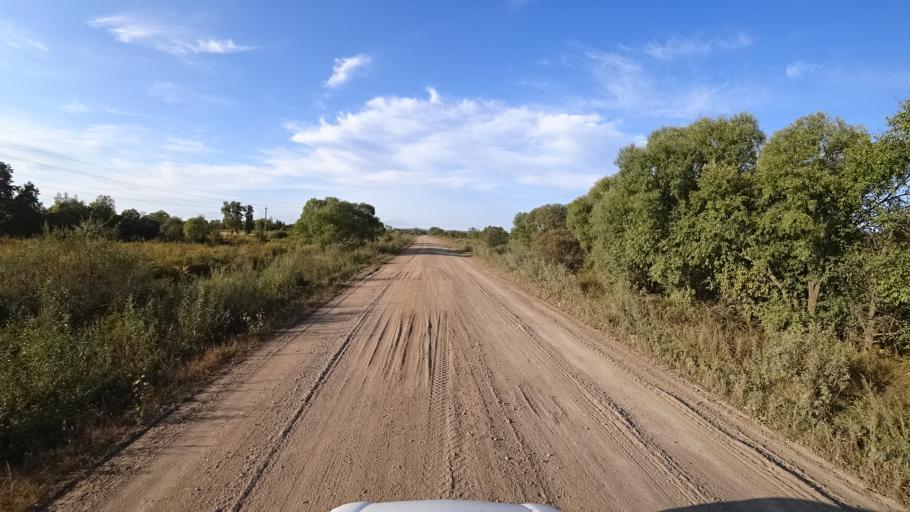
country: RU
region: Amur
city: Arkhara
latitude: 49.3575
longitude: 130.1372
